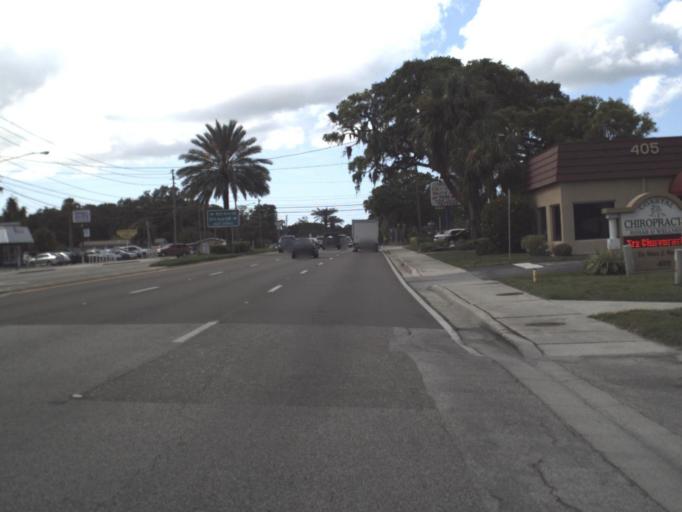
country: US
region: Florida
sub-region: Pinellas County
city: Largo
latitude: 27.9132
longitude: -82.7879
